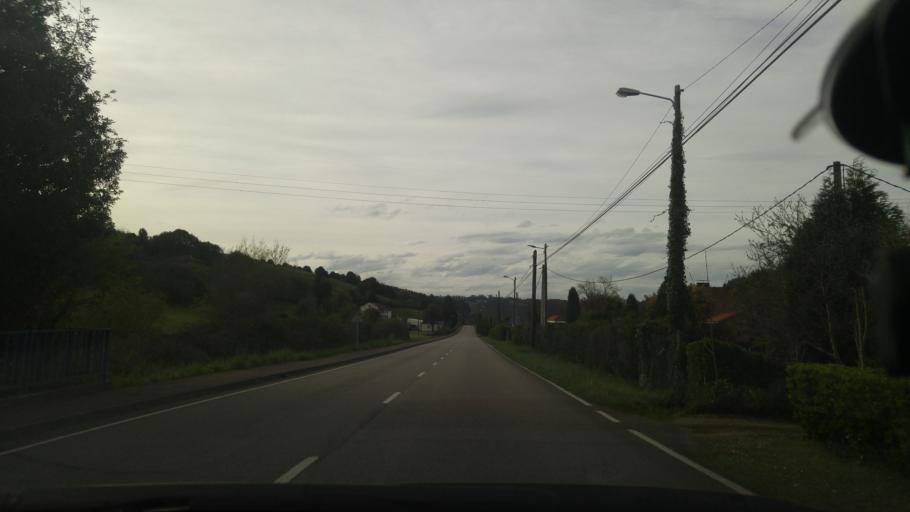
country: ES
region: Asturias
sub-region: Province of Asturias
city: Corvera de Asturias
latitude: 43.4929
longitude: -5.8514
